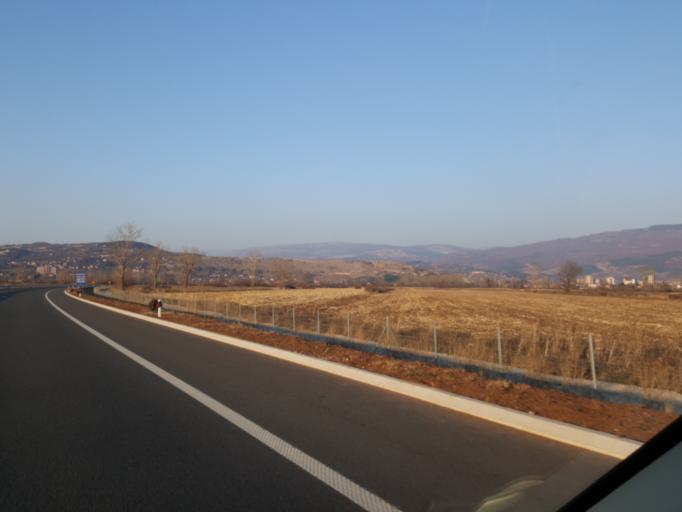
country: RS
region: Central Serbia
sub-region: Pirotski Okrug
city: Pirot
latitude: 43.1405
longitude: 22.5682
